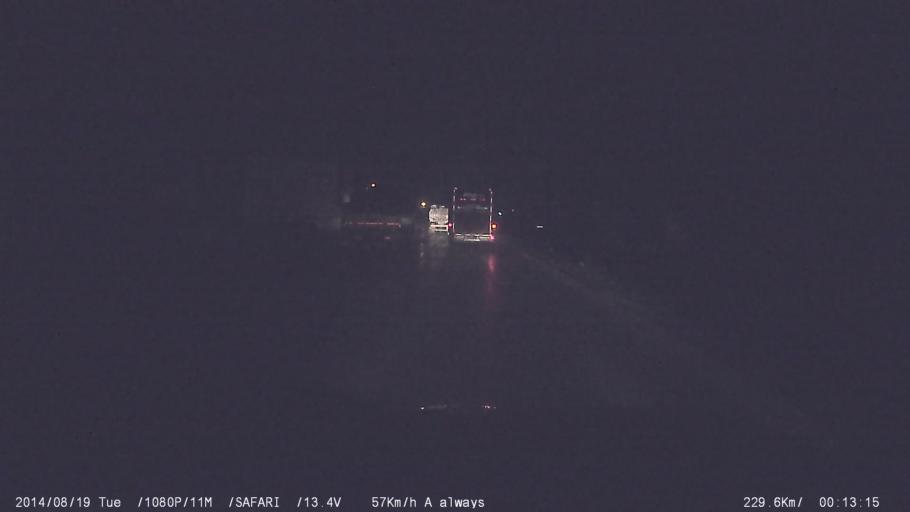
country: IN
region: Kerala
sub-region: Palakkad district
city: Palakkad
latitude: 10.7811
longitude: 76.7140
